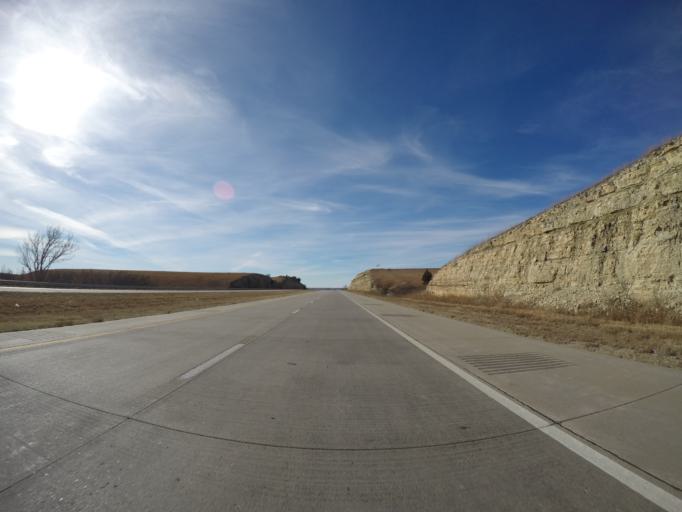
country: US
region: Kansas
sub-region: Riley County
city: Ogden
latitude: 39.0643
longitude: -96.6994
